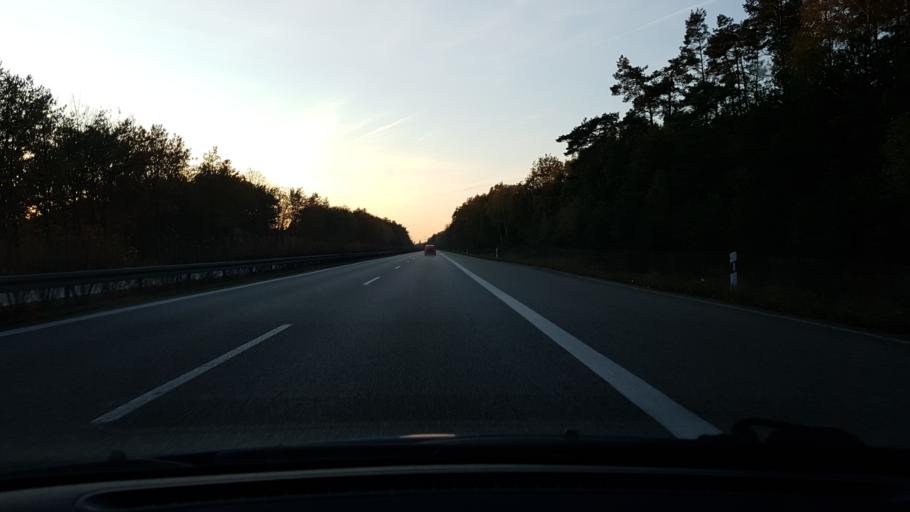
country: DE
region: Mecklenburg-Vorpommern
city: Zarrentin
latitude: 53.5086
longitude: 10.9884
